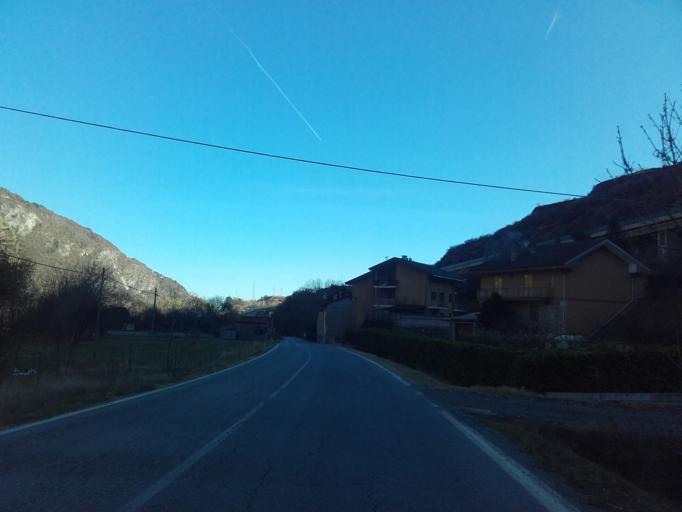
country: IT
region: Piedmont
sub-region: Provincia di Torino
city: Giaglione
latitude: 45.1466
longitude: 7.0272
